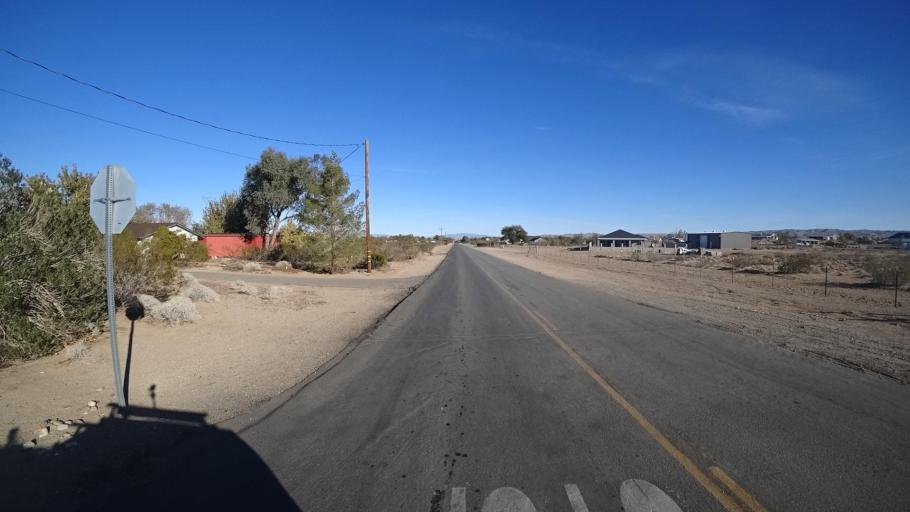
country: US
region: California
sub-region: Kern County
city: China Lake Acres
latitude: 35.6299
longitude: -117.7228
